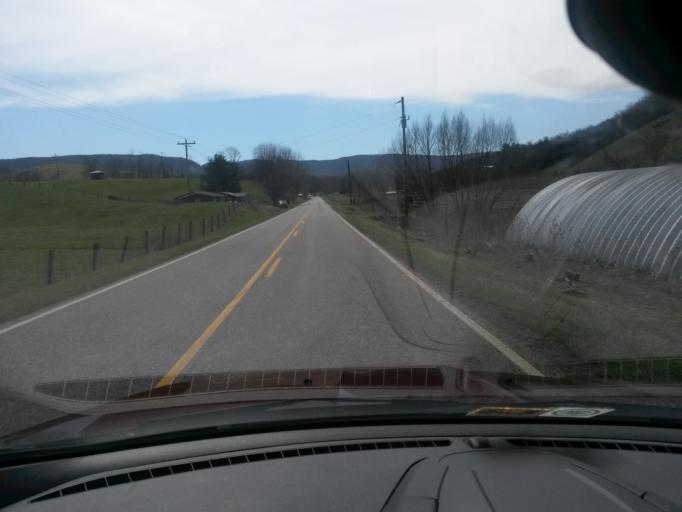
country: US
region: West Virginia
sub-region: Greenbrier County
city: White Sulphur Springs
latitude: 37.6494
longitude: -80.2363
